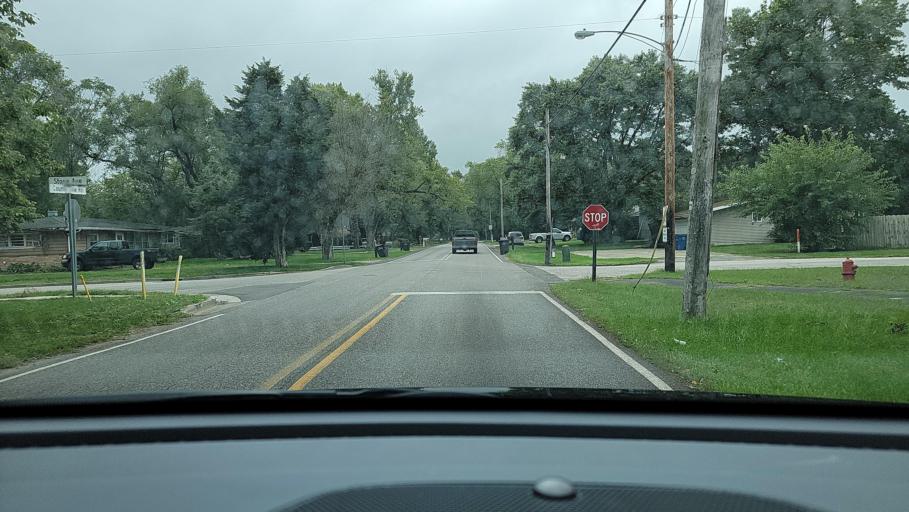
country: US
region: Indiana
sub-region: Lake County
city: Lake Station
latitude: 41.5653
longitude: -87.2218
